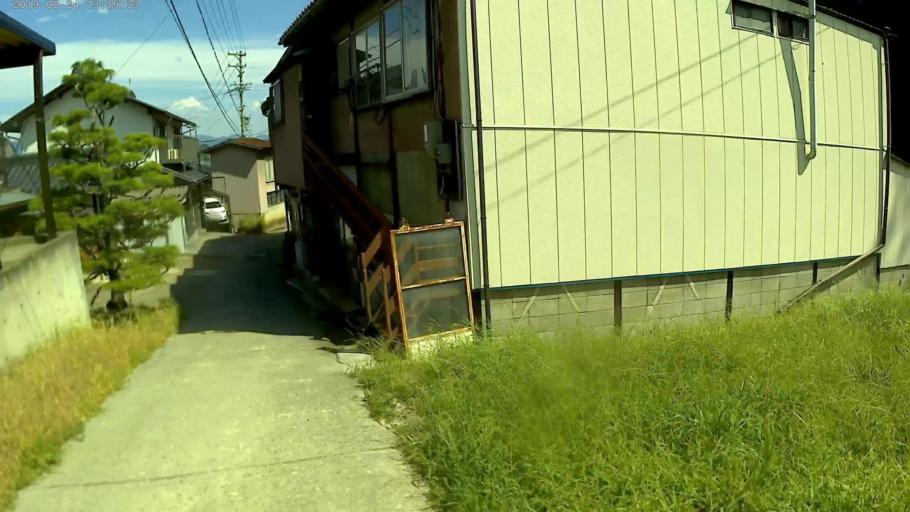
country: JP
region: Nagano
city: Komoro
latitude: 36.2720
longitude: 138.4137
